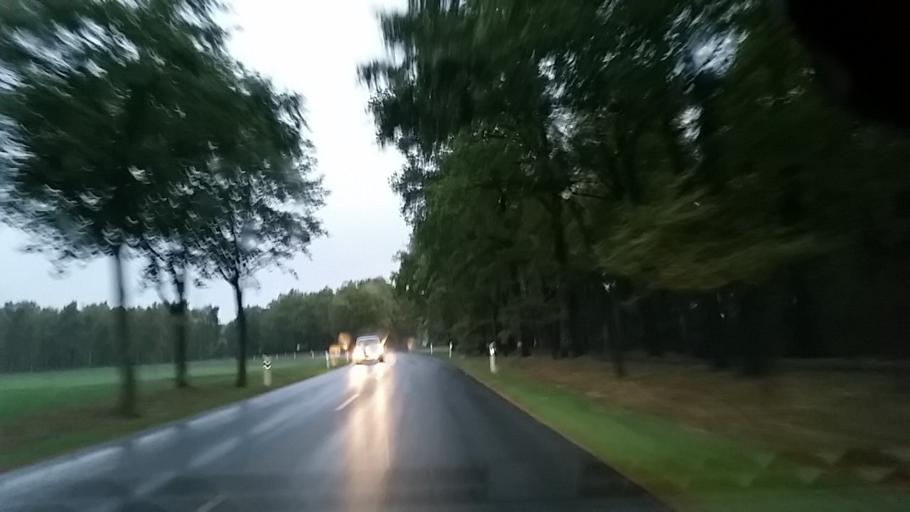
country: DE
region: Lower Saxony
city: Weyhausen
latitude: 52.4739
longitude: 10.7177
